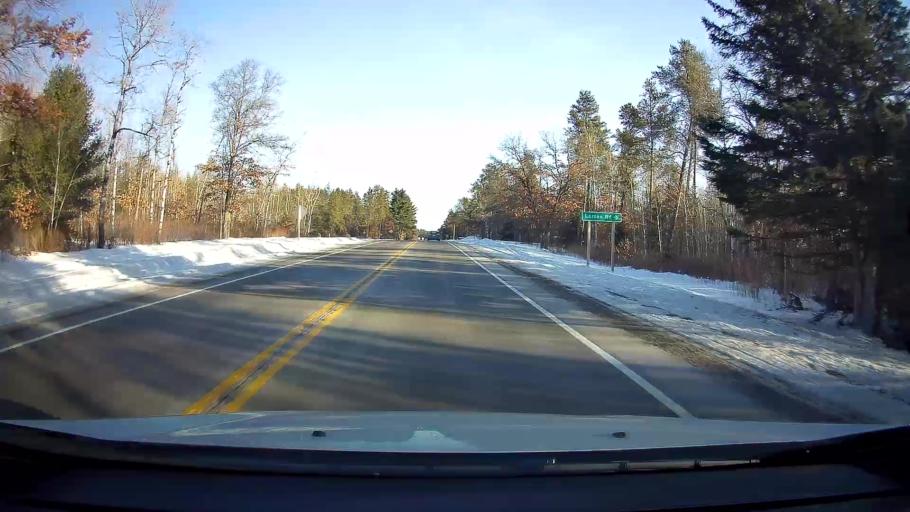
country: US
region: Wisconsin
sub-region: Sawyer County
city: Hayward
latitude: 45.9517
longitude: -91.6846
